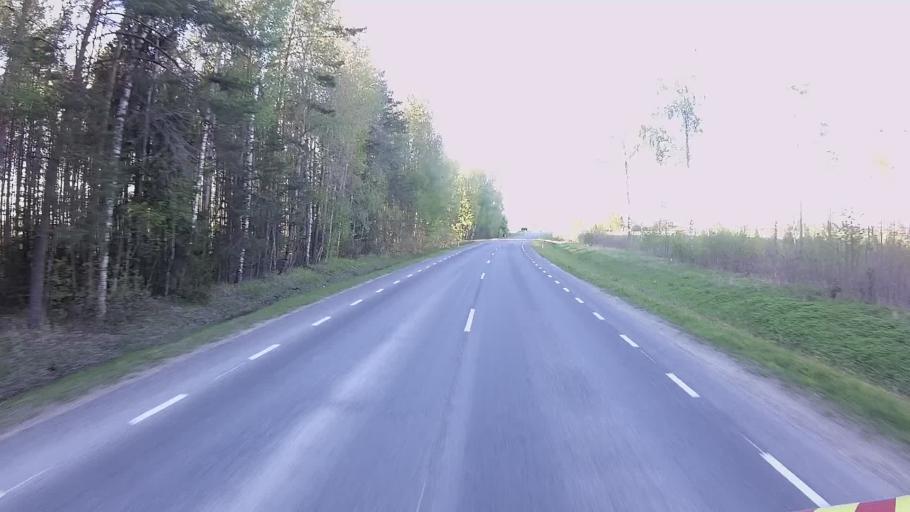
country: EE
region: Jogevamaa
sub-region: Poltsamaa linn
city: Poltsamaa
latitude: 58.5266
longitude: 25.8740
